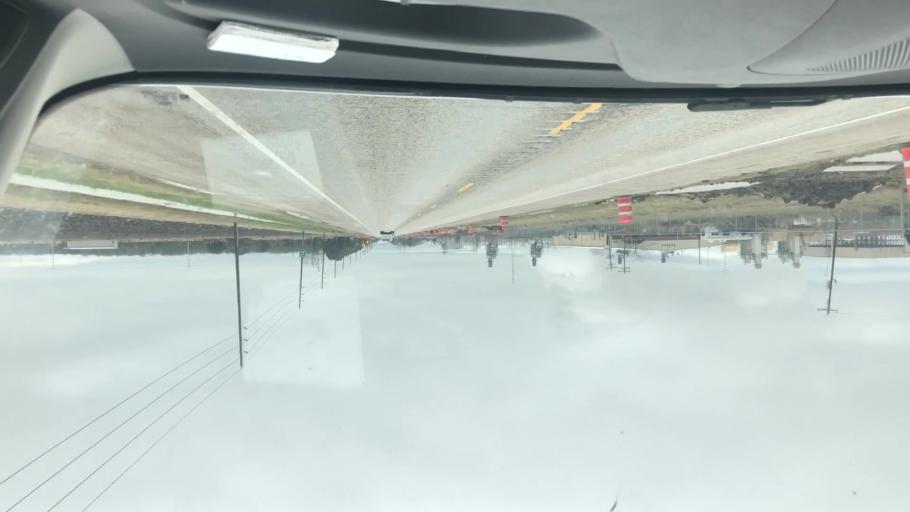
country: US
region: Texas
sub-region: Wharton County
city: Wharton
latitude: 29.2952
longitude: -96.0752
